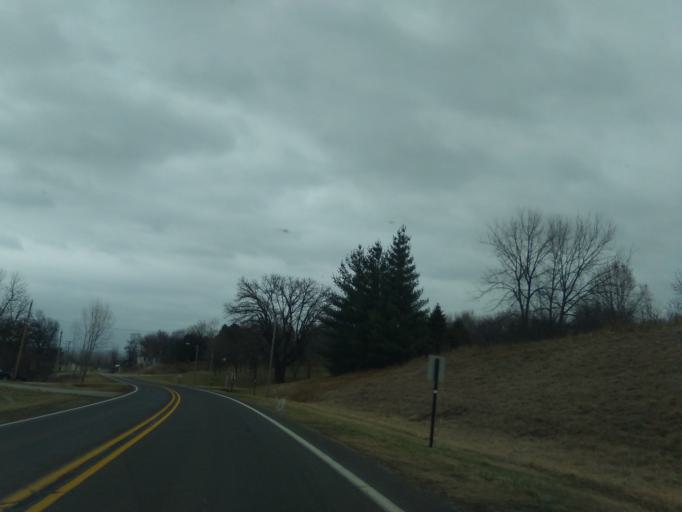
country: US
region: Nebraska
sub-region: Richardson County
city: Falls City
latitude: 40.0533
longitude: -95.4333
